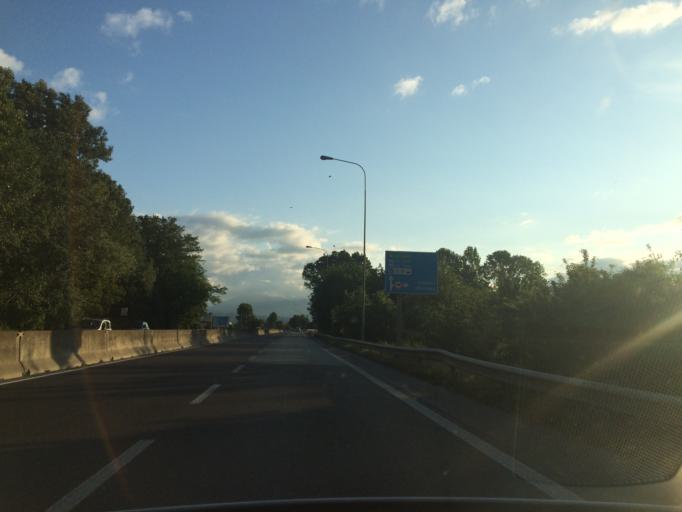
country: IT
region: Lombardy
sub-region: Provincia di Brescia
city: Castel Mella
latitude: 45.4988
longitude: 10.1620
